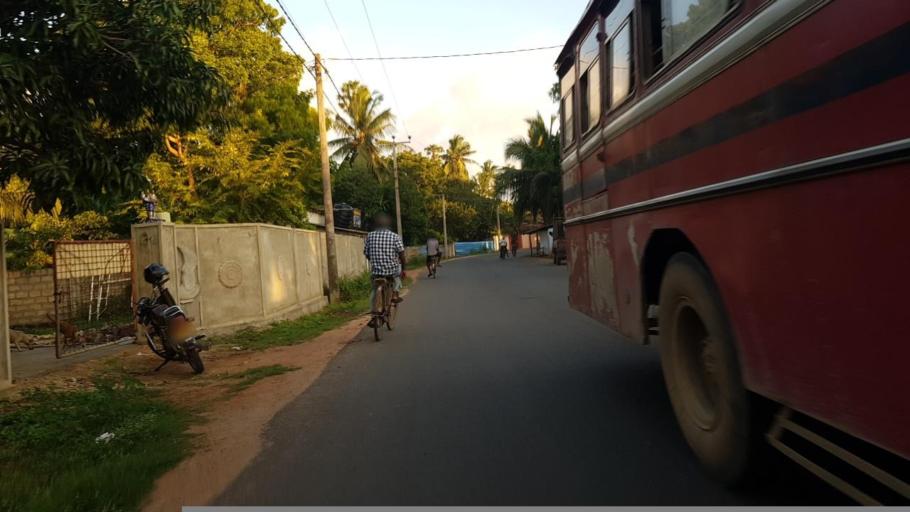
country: LK
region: Northern Province
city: Jaffna
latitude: 9.7166
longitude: 79.9836
